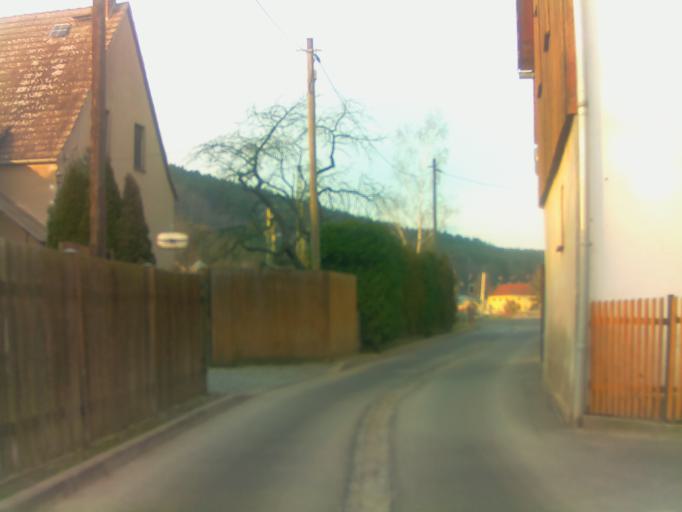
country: DE
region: Thuringia
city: Schops
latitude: 50.8347
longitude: 11.5978
